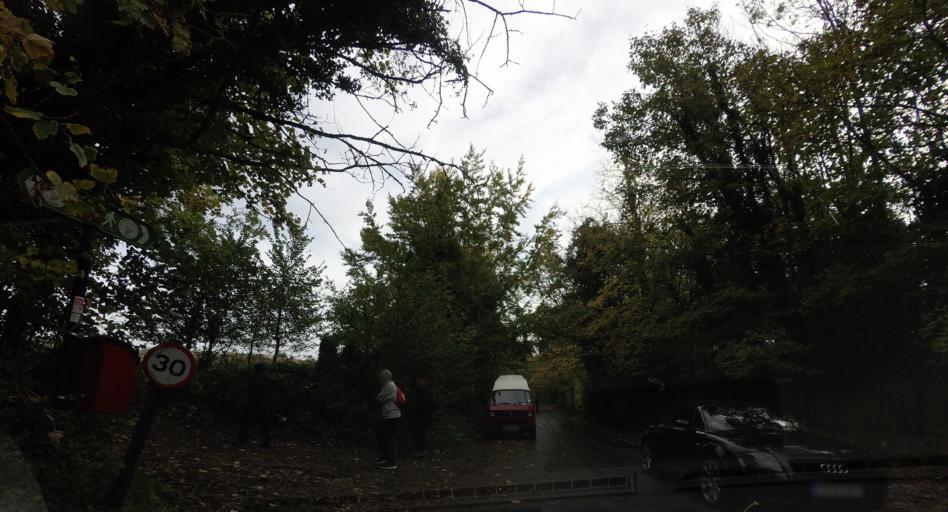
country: GB
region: England
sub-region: Kent
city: Shoreham
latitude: 51.3324
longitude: 0.1848
